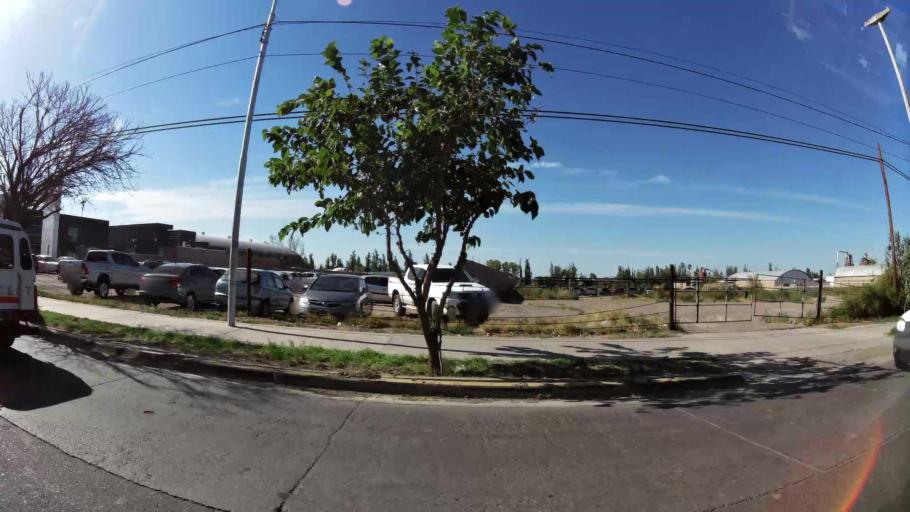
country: AR
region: Mendoza
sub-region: Departamento de Godoy Cruz
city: Godoy Cruz
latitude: -32.9278
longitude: -68.8169
